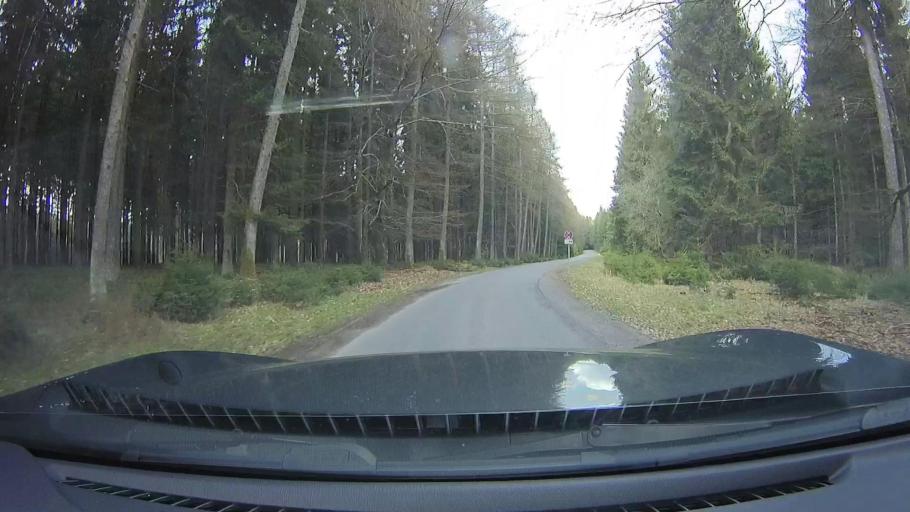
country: DE
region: Hesse
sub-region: Regierungsbezirk Darmstadt
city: Hesseneck
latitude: 49.6044
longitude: 9.0795
